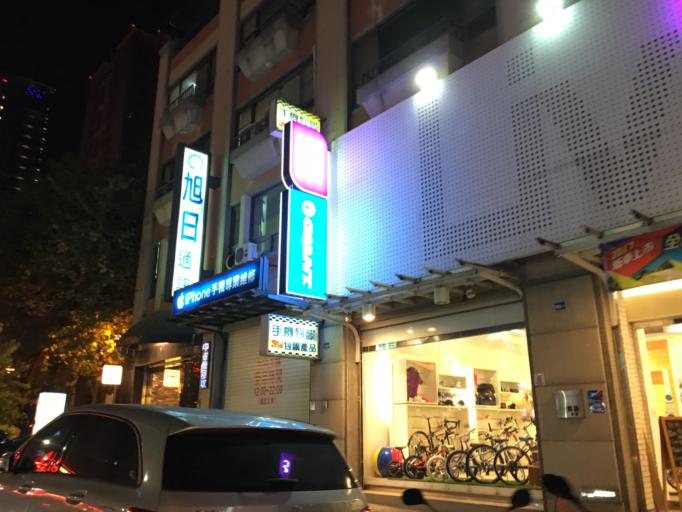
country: TW
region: Taiwan
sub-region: Taichung City
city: Taichung
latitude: 24.1905
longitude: 120.6122
